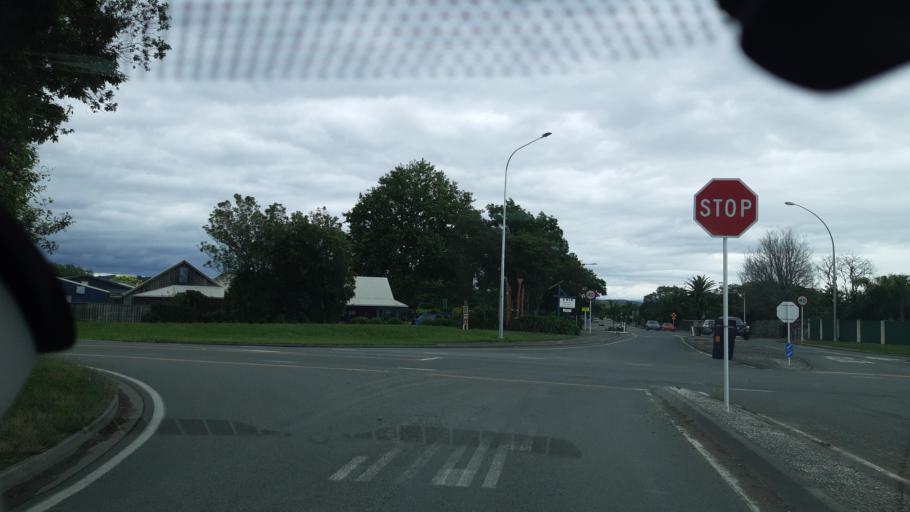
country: NZ
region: Tasman
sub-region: Tasman District
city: Brightwater
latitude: -41.3797
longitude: 173.1142
